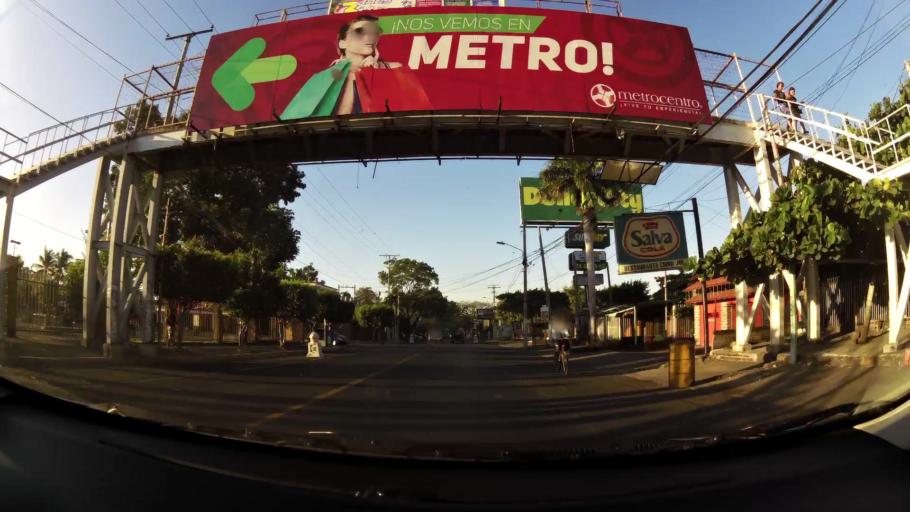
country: SV
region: Sonsonate
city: Sonsonate
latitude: 13.7135
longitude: -89.7260
